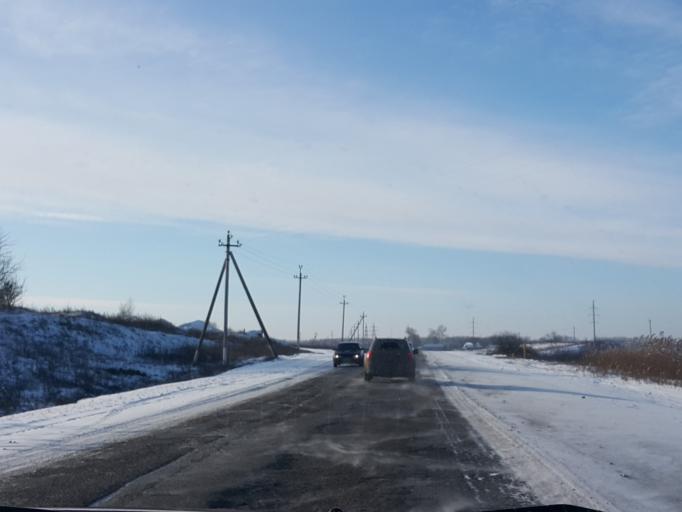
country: RU
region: Tambov
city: Znamenka
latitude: 52.4097
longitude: 41.4707
